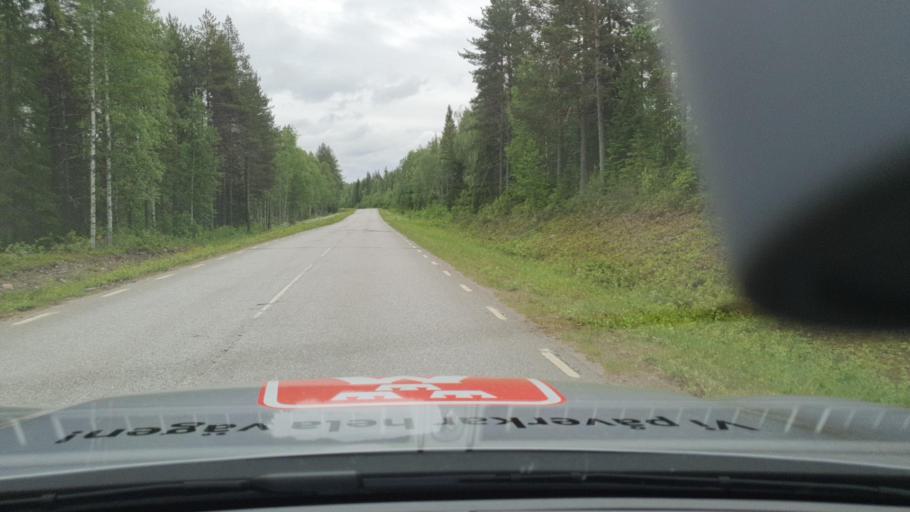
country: SE
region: Norrbotten
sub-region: Lulea Kommun
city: Ranea
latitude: 65.8887
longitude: 22.1926
